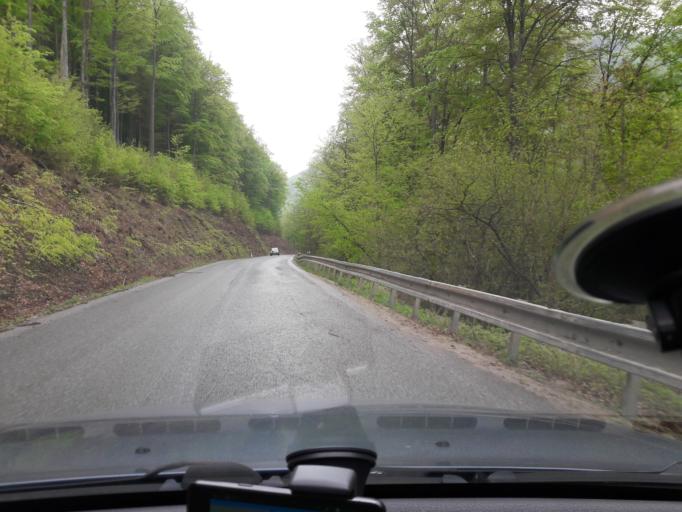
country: SK
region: Banskobystricky
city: Revuca
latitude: 48.7619
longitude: 20.0822
